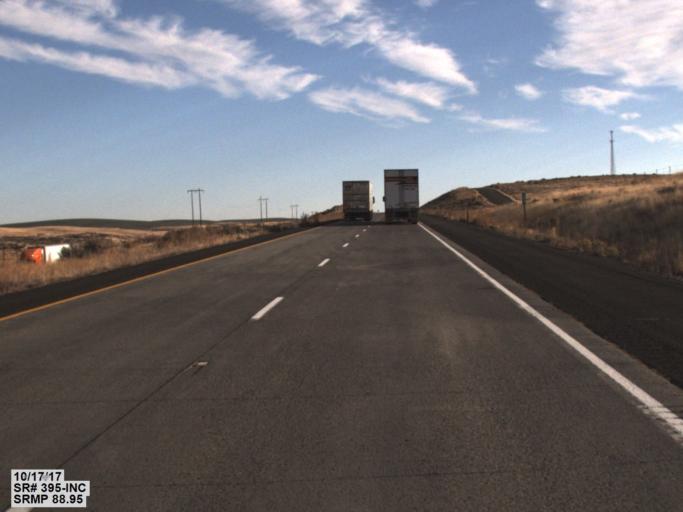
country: US
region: Washington
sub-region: Adams County
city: Ritzville
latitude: 47.0322
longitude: -118.4627
